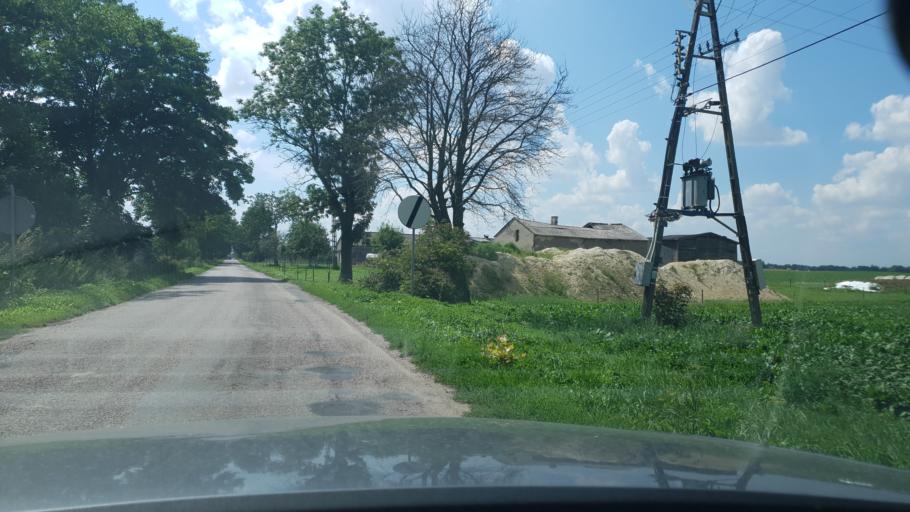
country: PL
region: Kujawsko-Pomorskie
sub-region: Powiat wabrzeski
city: Pluznica
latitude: 53.2637
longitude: 18.8348
